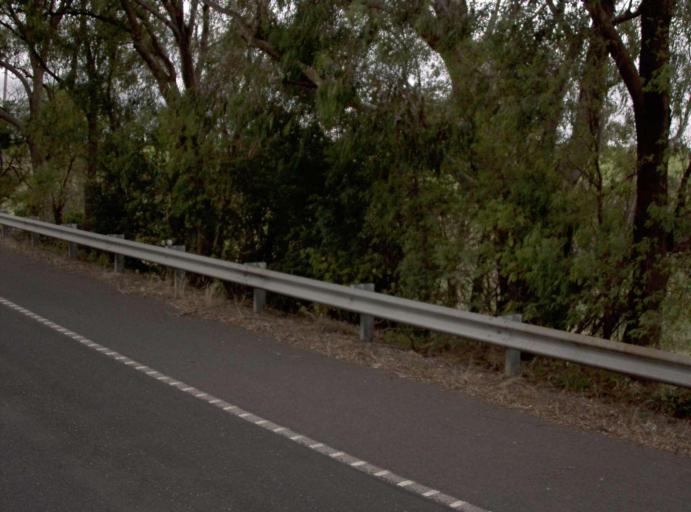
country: AU
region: Victoria
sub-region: Yarra Ranges
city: Badger Creek
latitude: -37.6834
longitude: 145.4534
